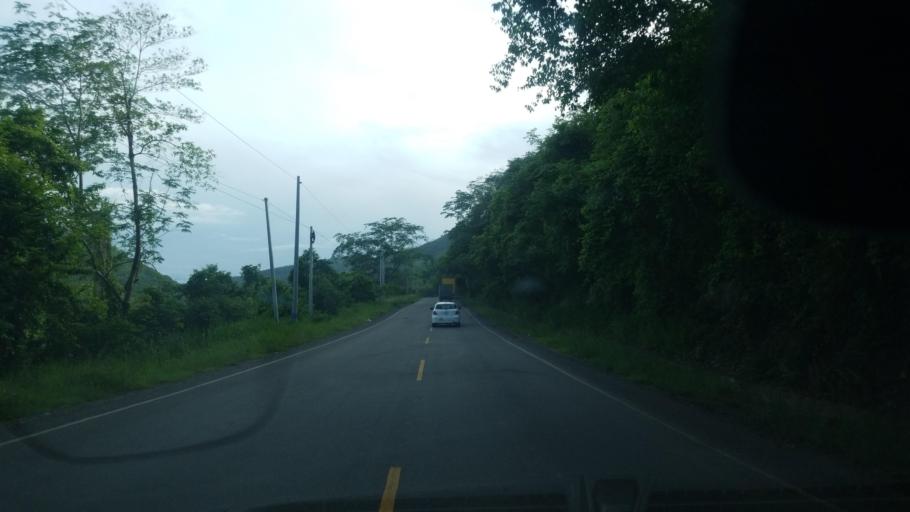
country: HN
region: Santa Barbara
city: Ilama
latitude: 15.0899
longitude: -88.2104
